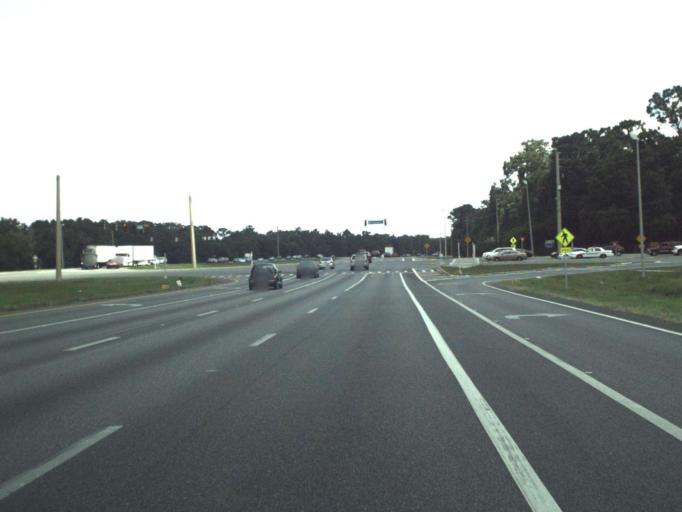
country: US
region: Florida
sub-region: Orange County
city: Fairview Shores
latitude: 28.5709
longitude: -81.4160
